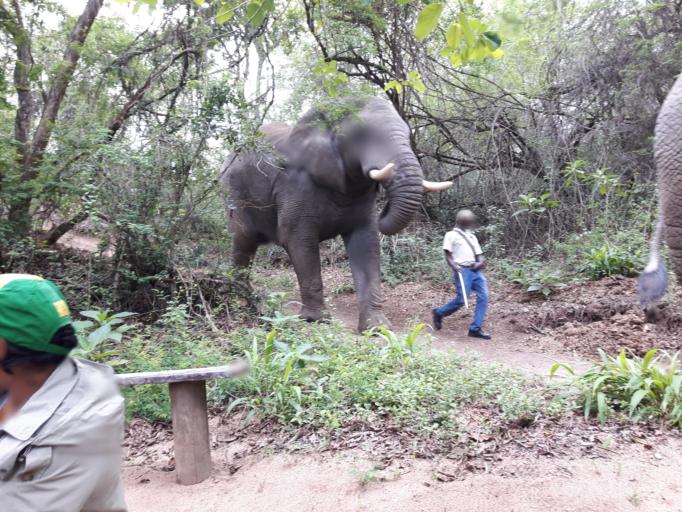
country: ZA
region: Mpumalanga
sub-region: Ehlanzeni District
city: Graksop
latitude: -25.0480
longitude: 31.0776
